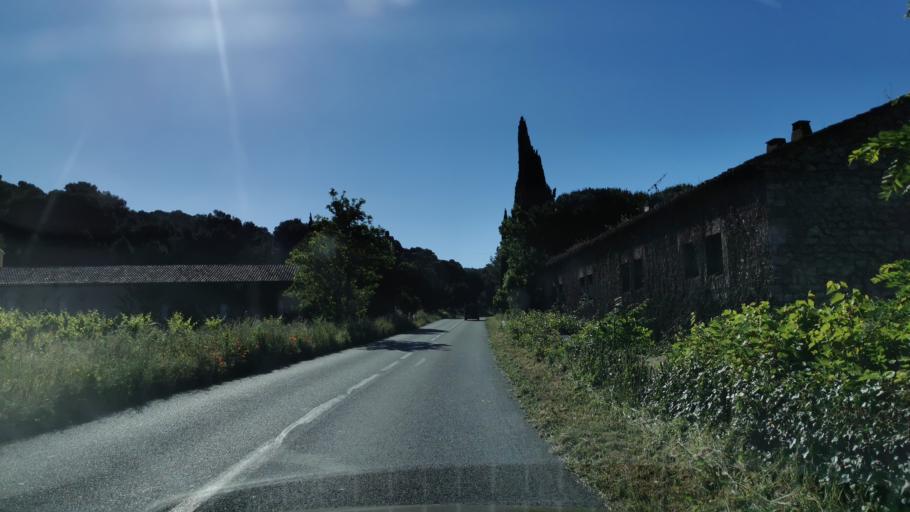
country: FR
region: Languedoc-Roussillon
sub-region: Departement de l'Aude
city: Vinassan
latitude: 43.1734
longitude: 3.0646
